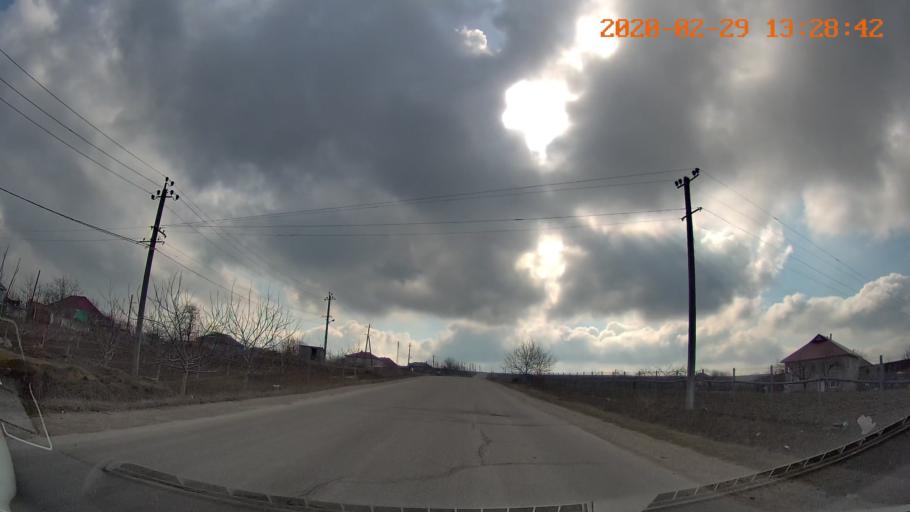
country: MD
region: Telenesti
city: Camenca
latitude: 47.9031
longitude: 28.6418
